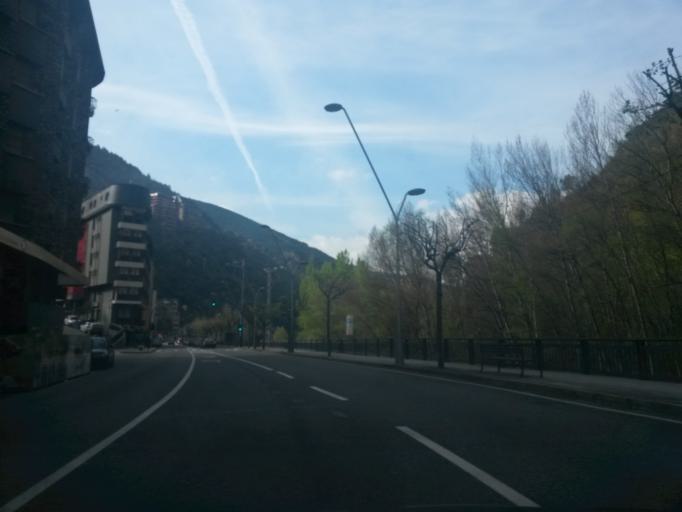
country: AD
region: Sant Julia de Loria
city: Sant Julia de Loria
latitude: 42.4647
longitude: 1.4898
